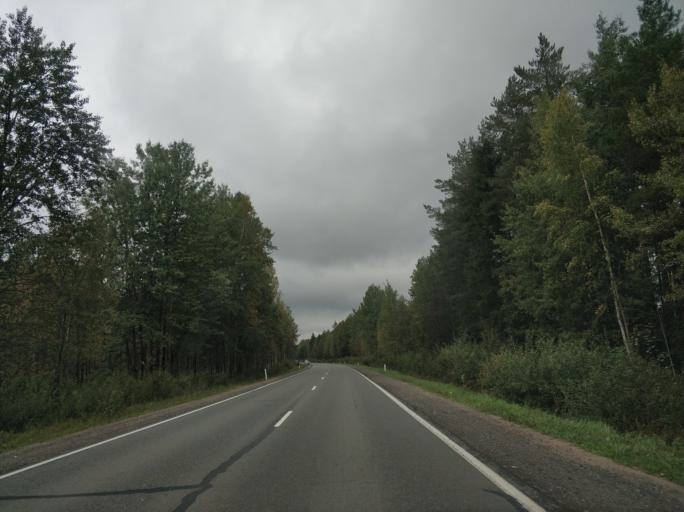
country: RU
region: Leningrad
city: Shcheglovo
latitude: 60.0996
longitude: 30.8370
